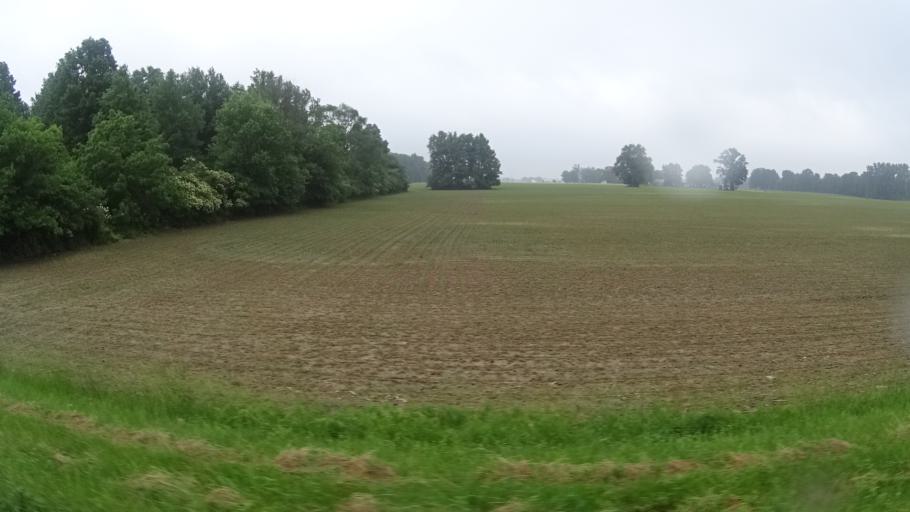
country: US
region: Ohio
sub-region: Huron County
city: Bellevue
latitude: 41.3264
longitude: -82.8404
